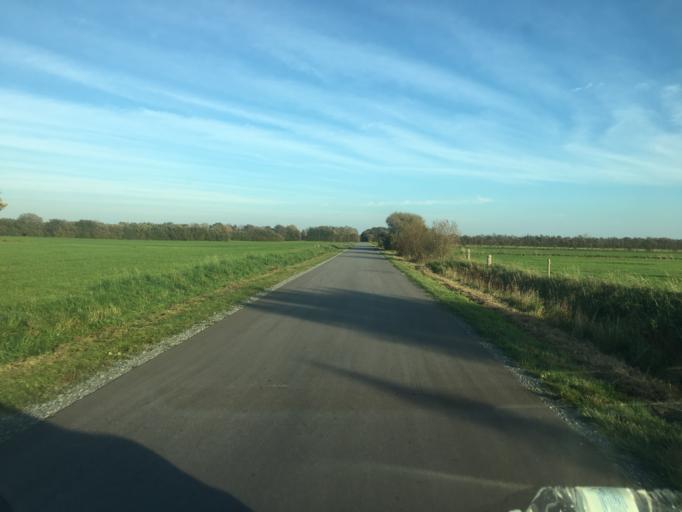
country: DE
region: Schleswig-Holstein
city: Bramstedtlund
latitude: 54.8946
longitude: 9.0470
